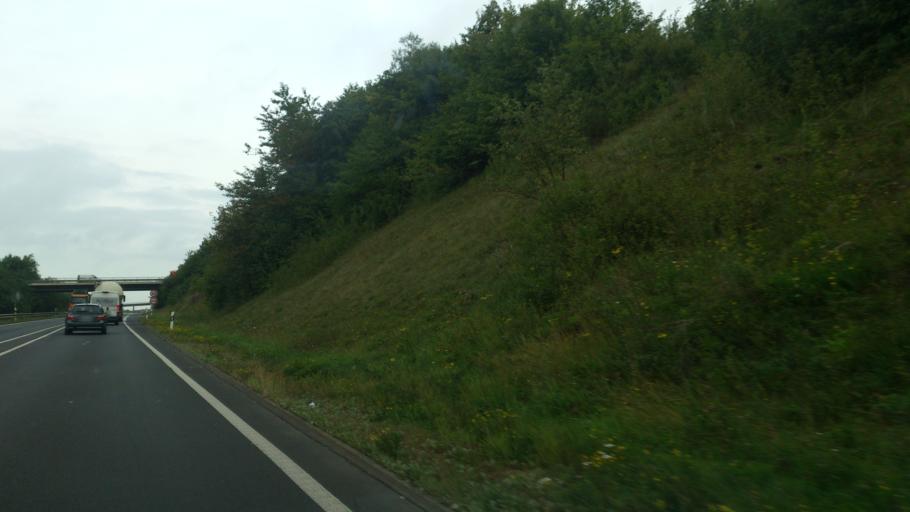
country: DE
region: North Rhine-Westphalia
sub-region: Regierungsbezirk Koln
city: Blankenheim
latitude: 50.4626
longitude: 6.6998
